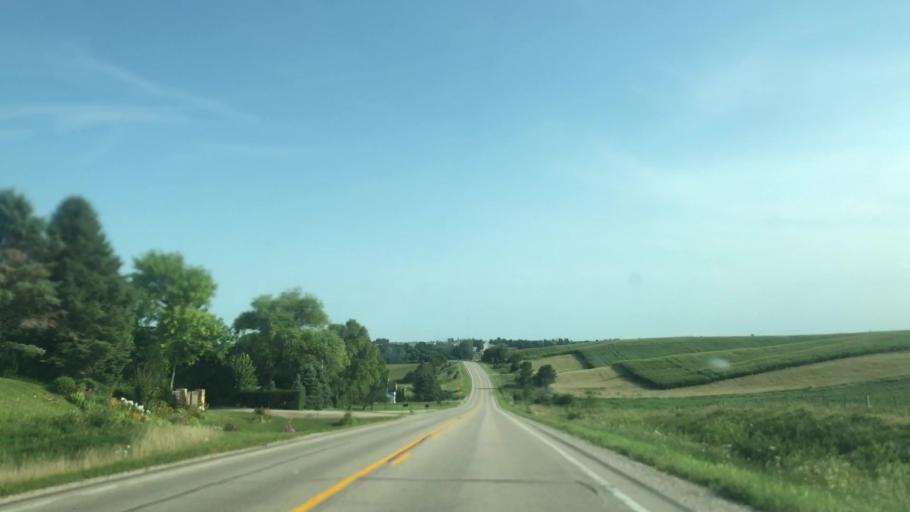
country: US
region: Iowa
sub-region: Marshall County
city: Marshalltown
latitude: 42.0402
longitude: -93.0001
